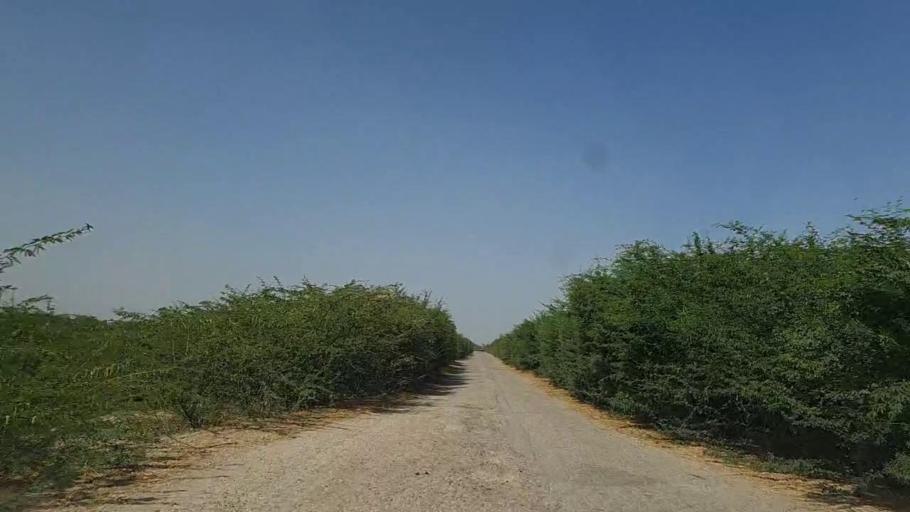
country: PK
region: Sindh
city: Naukot
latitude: 24.6473
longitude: 69.2879
